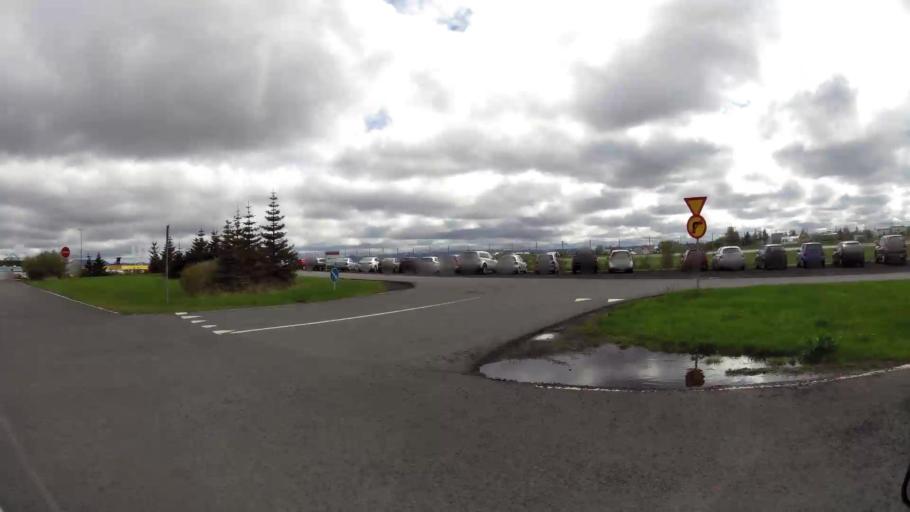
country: IS
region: Capital Region
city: Kopavogur
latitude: 64.1324
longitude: -21.9497
